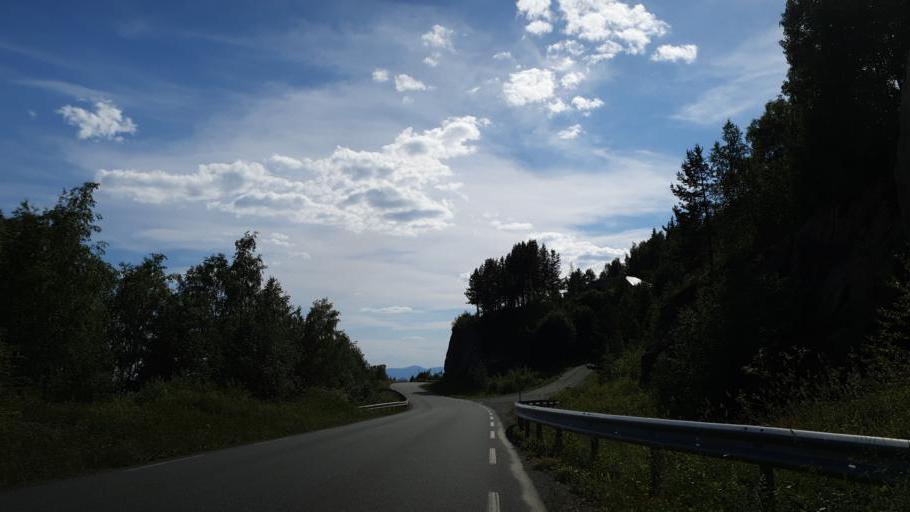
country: NO
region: Nord-Trondelag
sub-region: Leksvik
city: Leksvik
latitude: 63.6226
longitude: 10.5302
